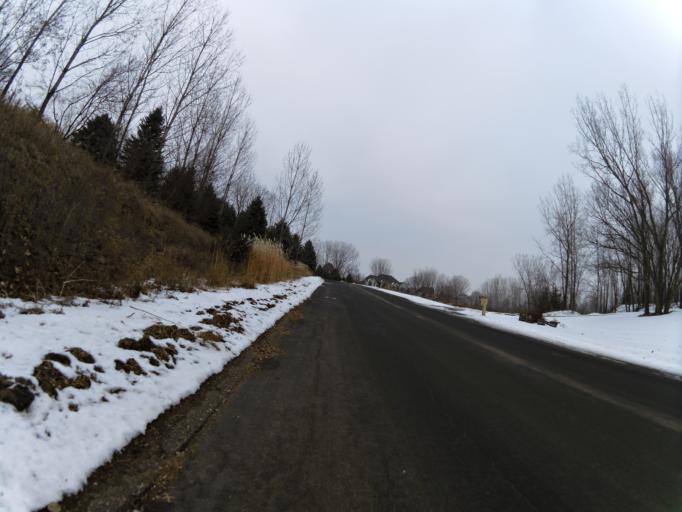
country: US
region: Minnesota
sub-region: Washington County
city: Lake Elmo
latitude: 44.9704
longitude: -92.8440
